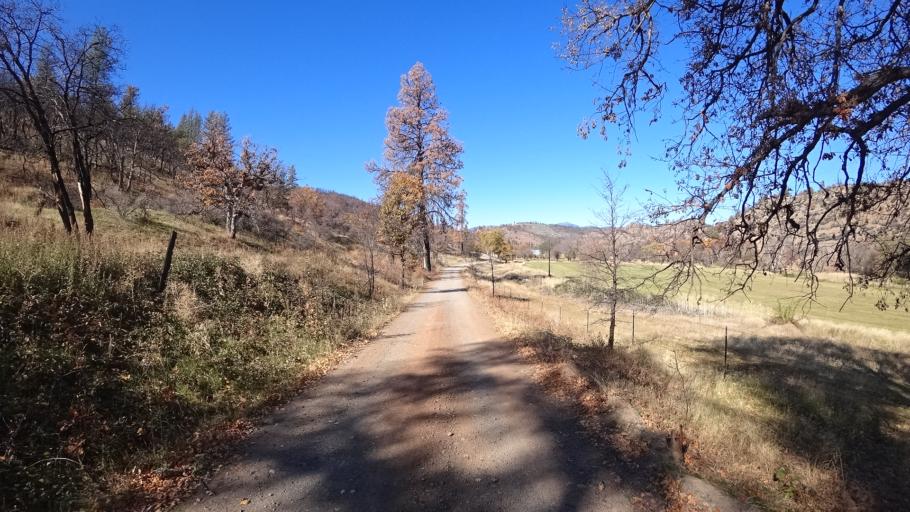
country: US
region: California
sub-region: Siskiyou County
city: Yreka
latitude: 41.9435
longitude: -122.5956
